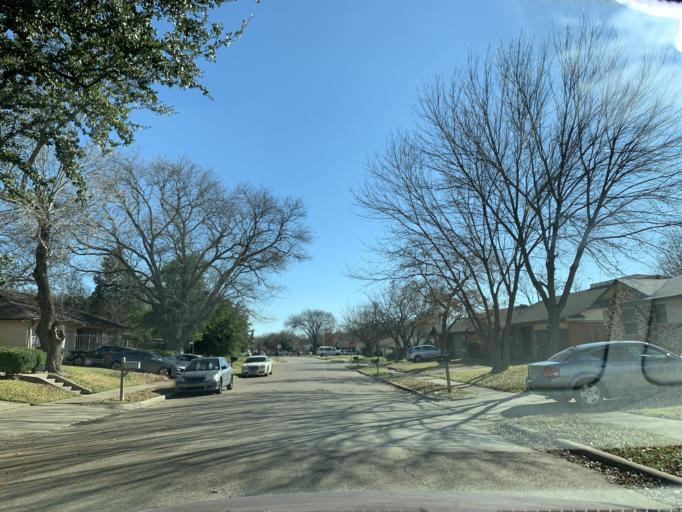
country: US
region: Texas
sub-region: Tarrant County
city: Arlington
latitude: 32.7310
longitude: -97.0681
